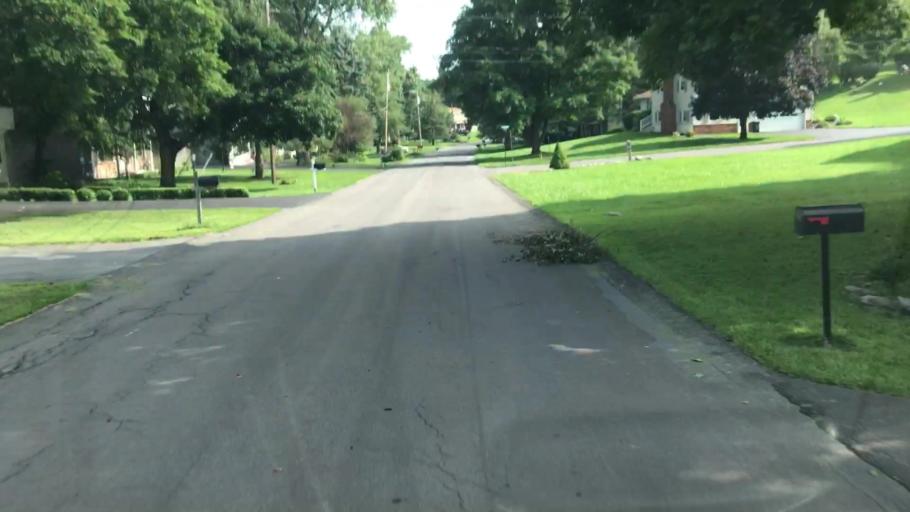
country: US
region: New York
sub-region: Onondaga County
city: Manlius
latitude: 42.9932
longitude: -75.9875
